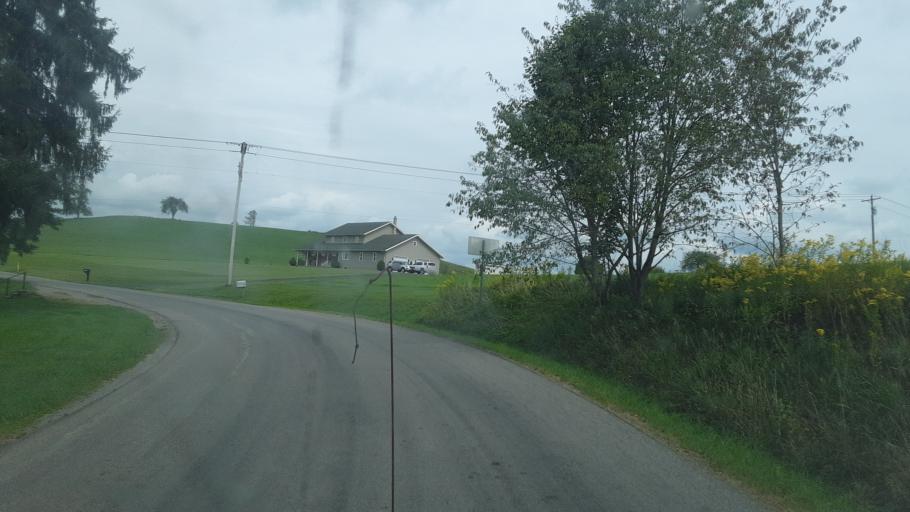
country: US
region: Pennsylvania
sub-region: Jefferson County
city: Punxsutawney
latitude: 40.9570
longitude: -79.1070
